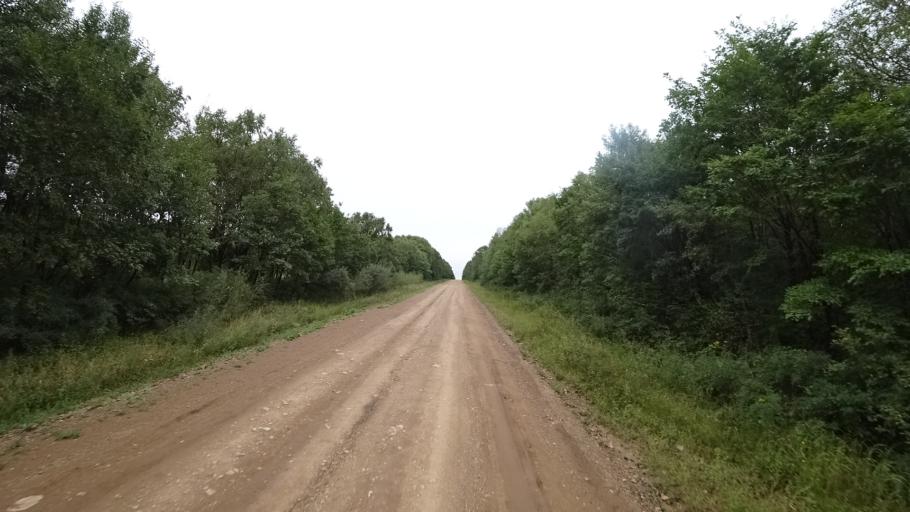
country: RU
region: Primorskiy
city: Ivanovka
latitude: 44.0278
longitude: 132.5269
